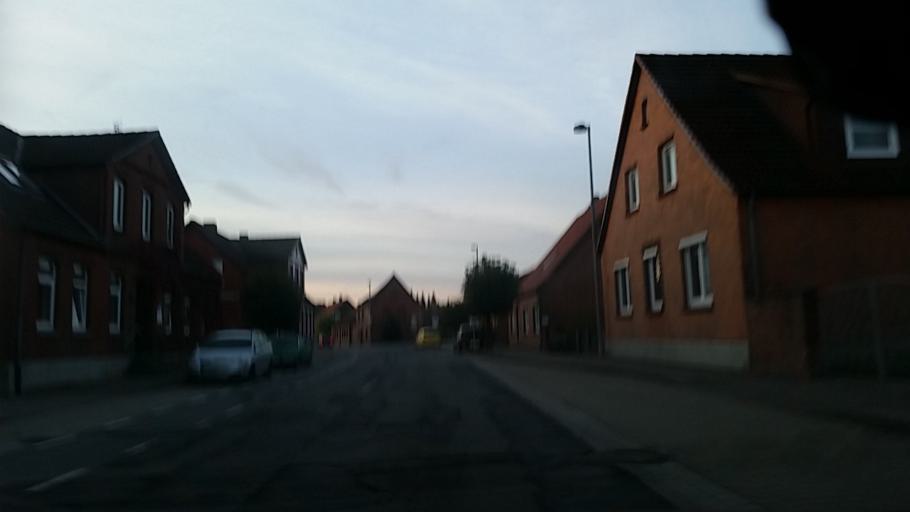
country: DE
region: Lower Saxony
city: Bodenteich
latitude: 52.8309
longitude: 10.6821
